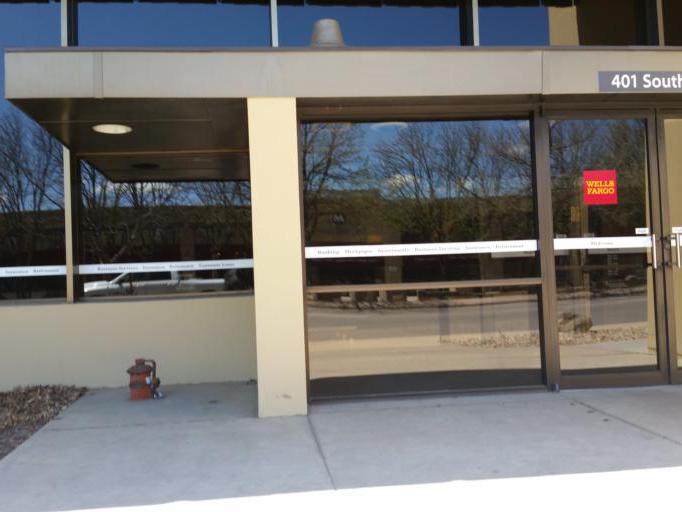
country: US
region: Colorado
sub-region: Larimer County
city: Fort Collins
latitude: 40.5824
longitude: -105.0773
